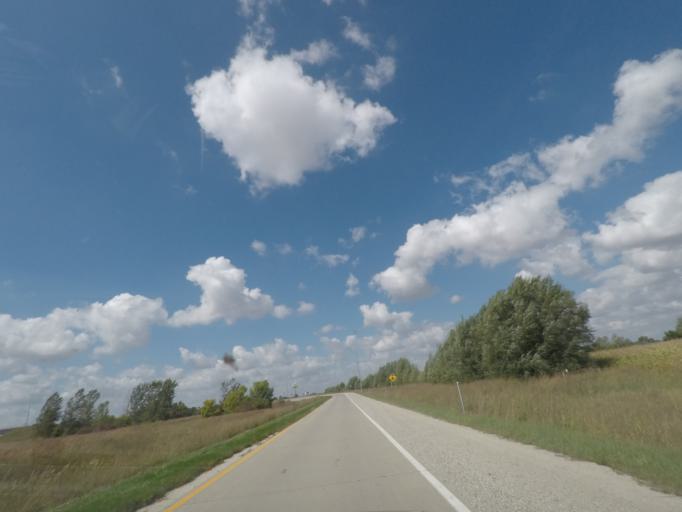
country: US
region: Iowa
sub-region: Story County
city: Nevada
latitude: 42.0088
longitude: -93.4313
